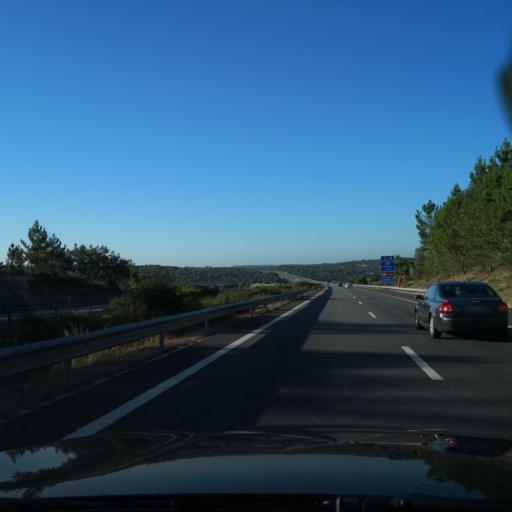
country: PT
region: Setubal
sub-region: Alcacer do Sal
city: Alcacer do Sal
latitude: 38.4416
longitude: -8.5243
